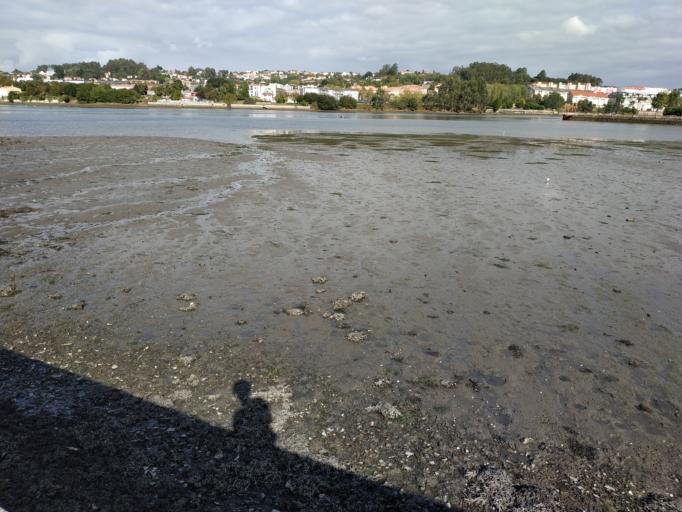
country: ES
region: Galicia
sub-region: Provincia da Coruna
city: Cambre
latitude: 43.3206
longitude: -8.3704
